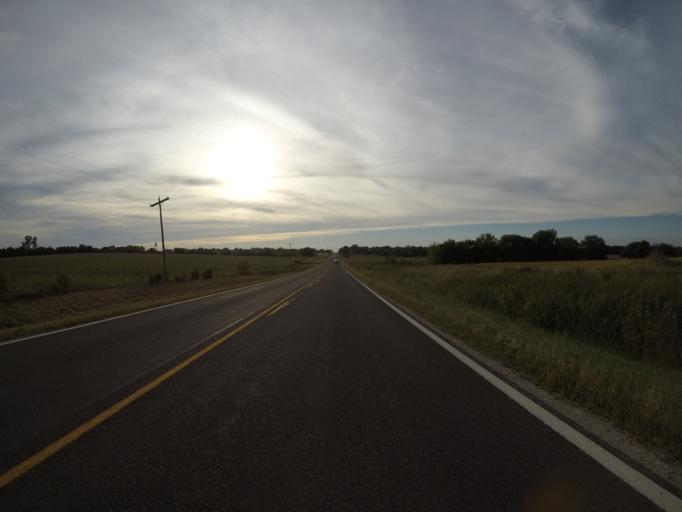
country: US
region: Kansas
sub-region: Osage County
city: Overbrook
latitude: 38.7824
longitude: -95.5430
